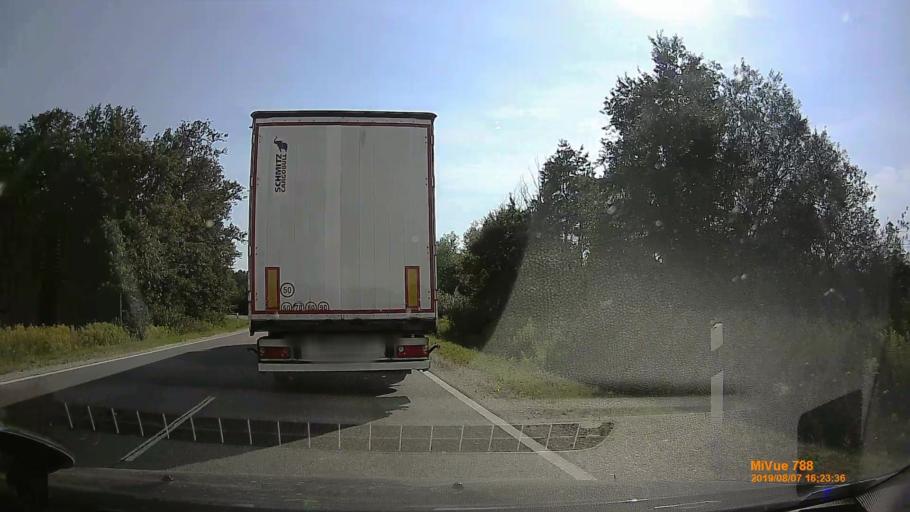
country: HU
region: Zala
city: Zalalovo
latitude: 46.7461
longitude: 16.5557
